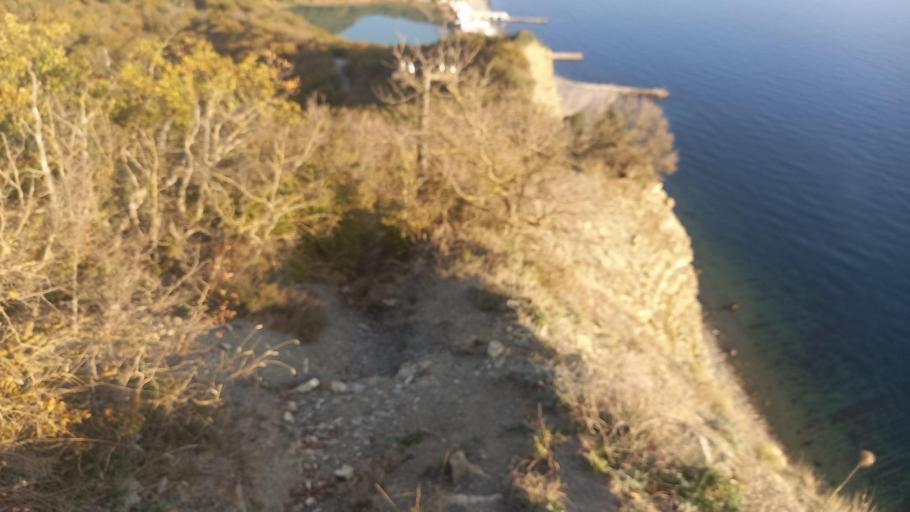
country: RU
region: Krasnodarskiy
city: Abrau-Dyurso
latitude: 44.6709
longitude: 37.5848
